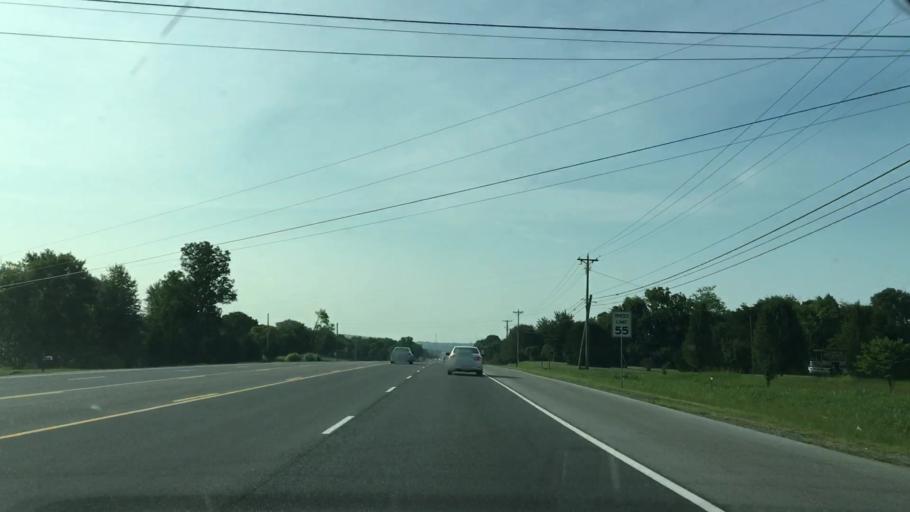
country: US
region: Tennessee
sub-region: Wilson County
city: Mount Juliet
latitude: 36.2067
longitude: -86.4190
